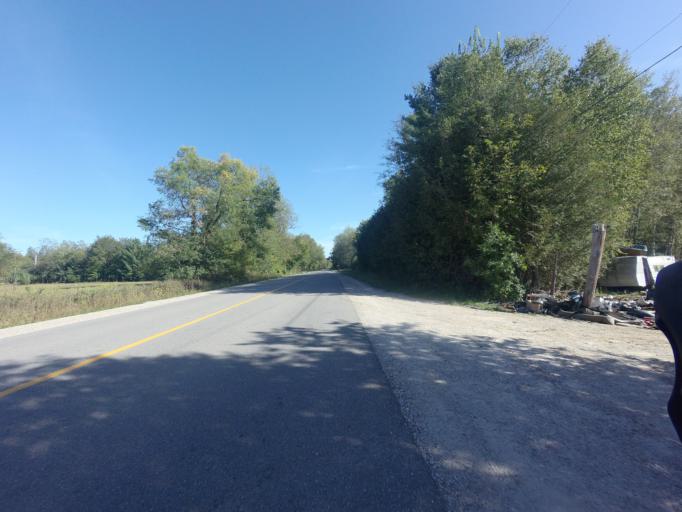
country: CA
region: Ontario
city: Perth
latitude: 44.9018
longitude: -76.3324
